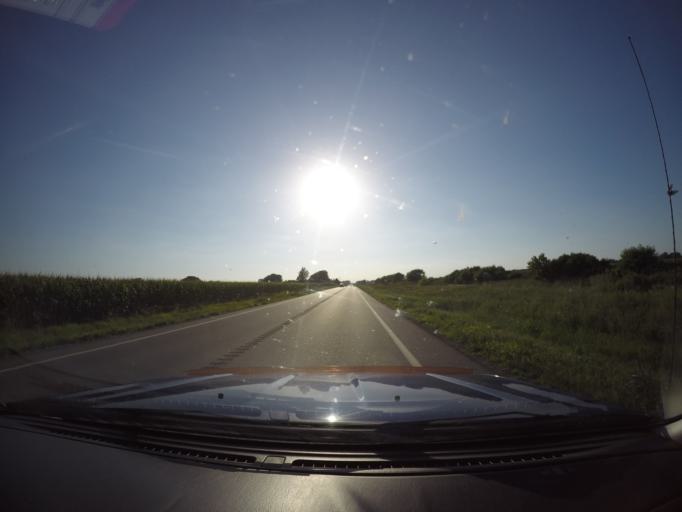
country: US
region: Kansas
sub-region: Shawnee County
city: Silver Lake
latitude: 39.1135
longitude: -95.8924
